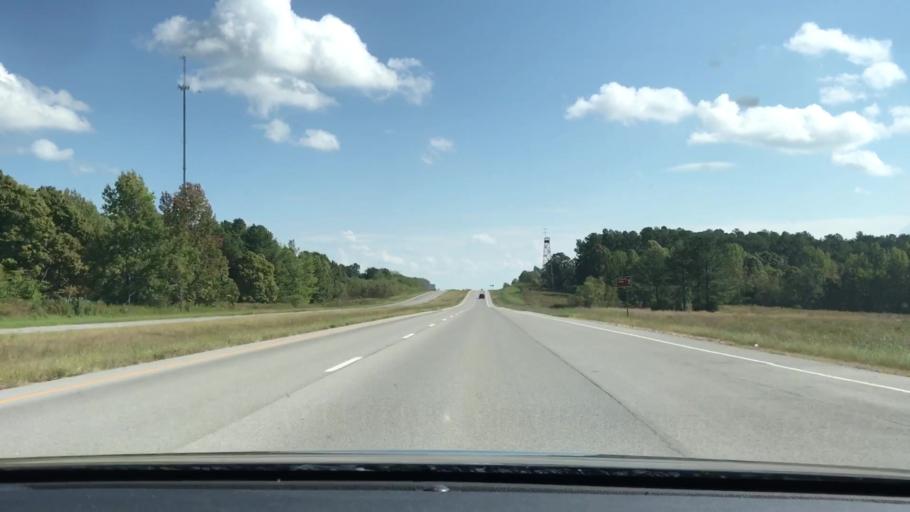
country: US
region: Kentucky
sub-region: Trigg County
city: Cadiz
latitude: 36.7798
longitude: -88.0622
